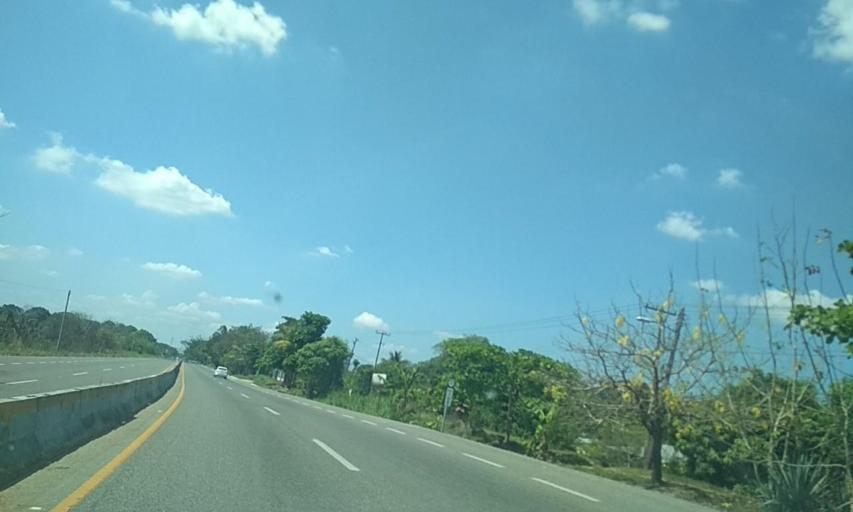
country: MX
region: Tabasco
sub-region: Huimanguillo
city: El Dorado
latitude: 17.8869
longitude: -93.3666
